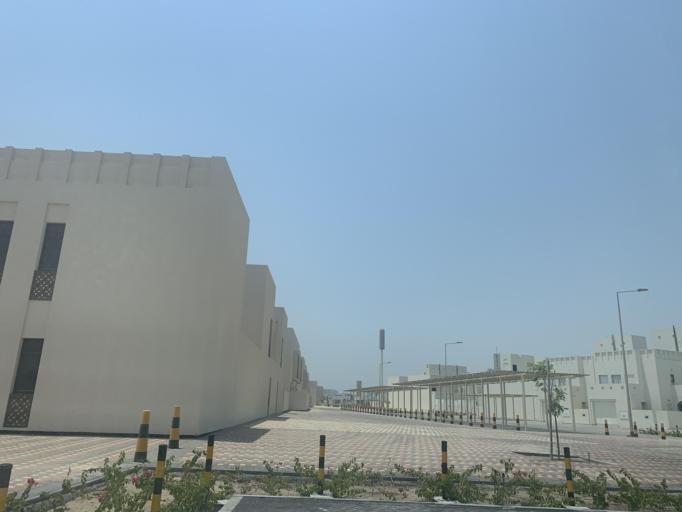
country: BH
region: Muharraq
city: Al Hadd
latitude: 26.2382
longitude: 50.6691
